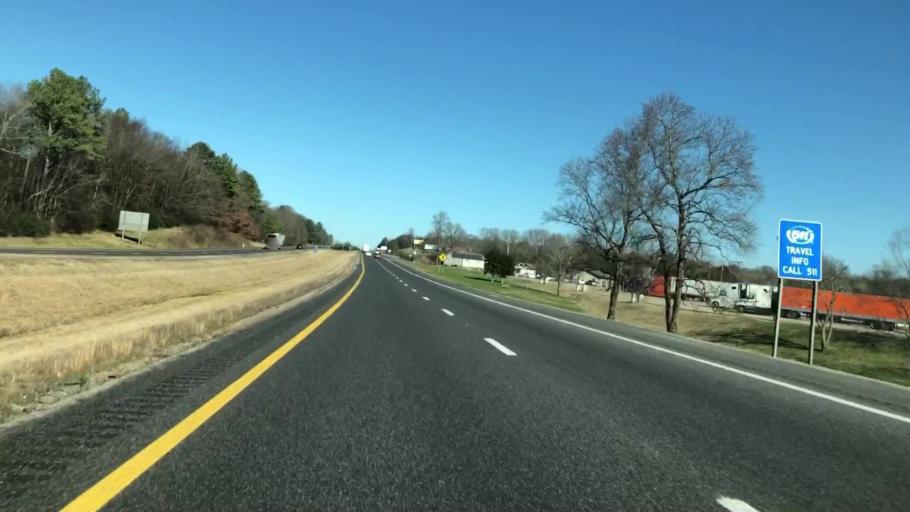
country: US
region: Alabama
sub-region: Limestone County
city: Ardmore
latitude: 35.0343
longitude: -86.8786
